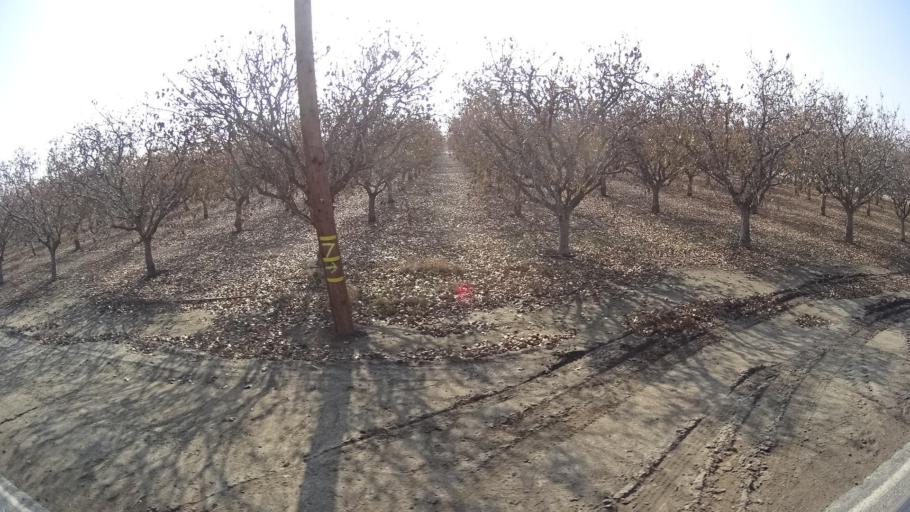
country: US
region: California
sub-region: Kern County
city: Buttonwillow
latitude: 35.3546
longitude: -119.4168
